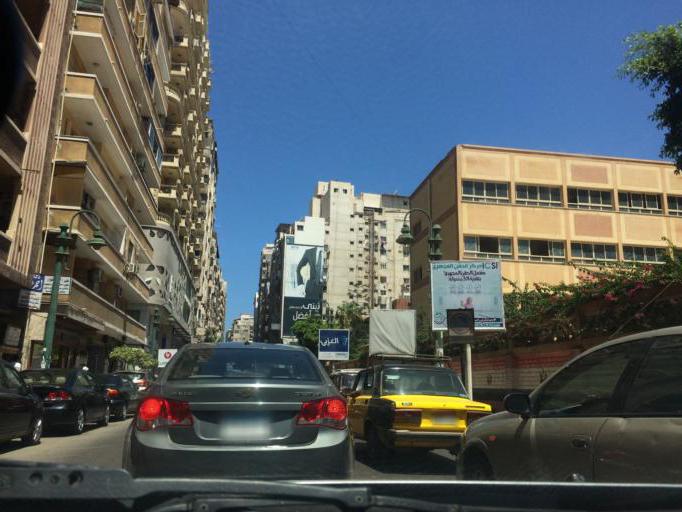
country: EG
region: Alexandria
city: Alexandria
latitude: 31.2293
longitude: 29.9508
